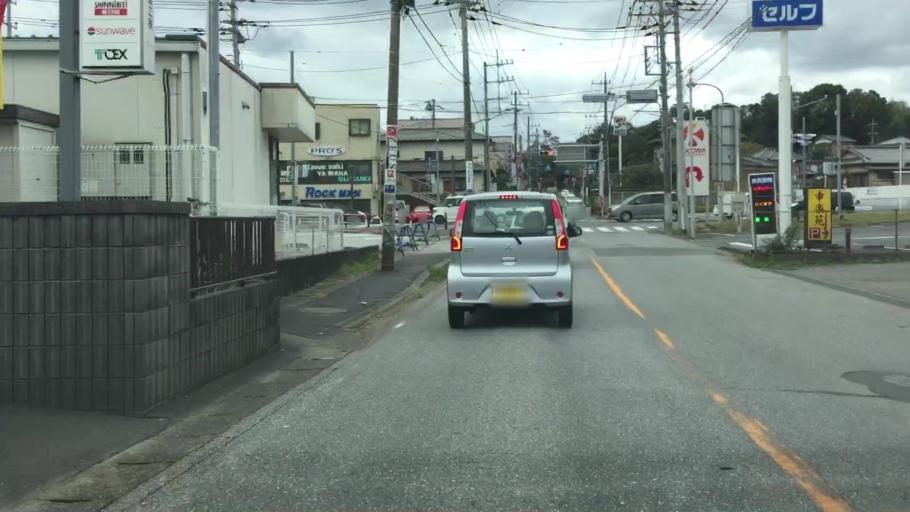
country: JP
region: Ibaraki
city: Ryugasaki
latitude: 35.8349
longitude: 140.1436
